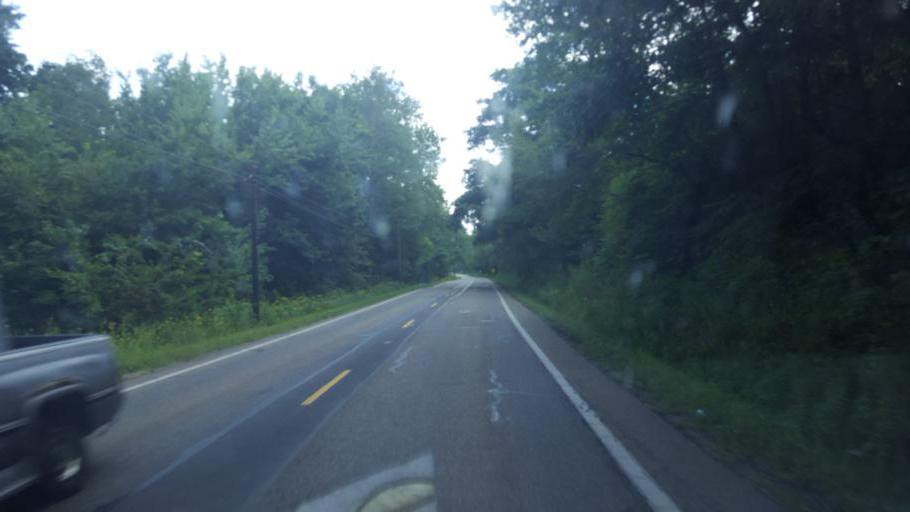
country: US
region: Ohio
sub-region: Tuscarawas County
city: Dover
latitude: 40.5350
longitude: -81.4312
